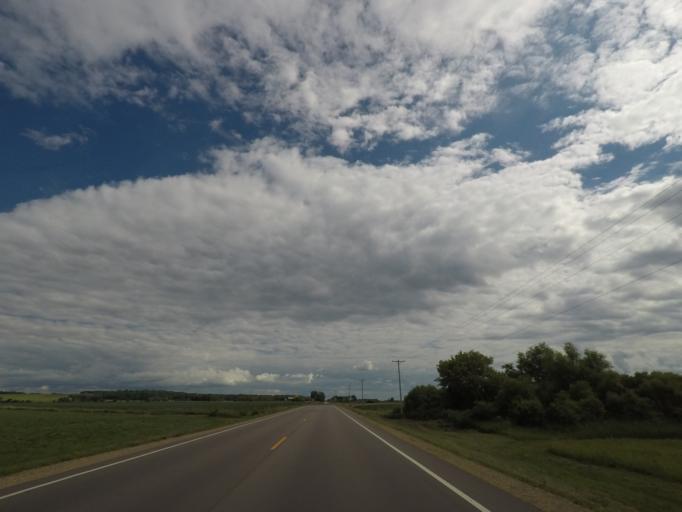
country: US
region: Wisconsin
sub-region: Green County
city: Albany
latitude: 42.7223
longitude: -89.3683
